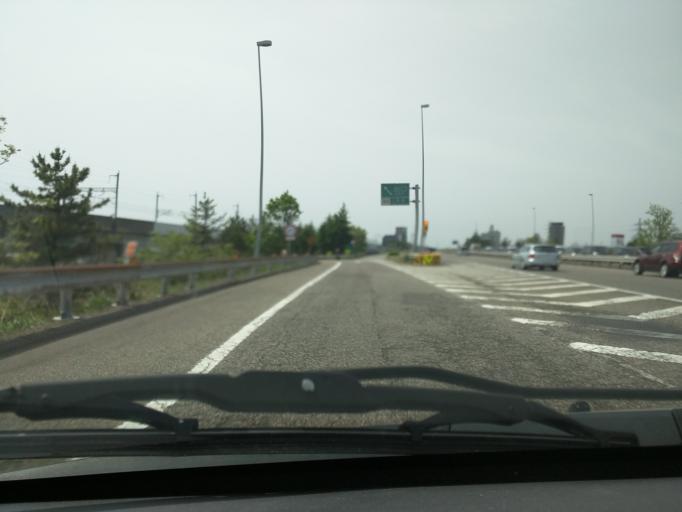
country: JP
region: Niigata
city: Tsubame
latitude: 37.6538
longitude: 138.9409
